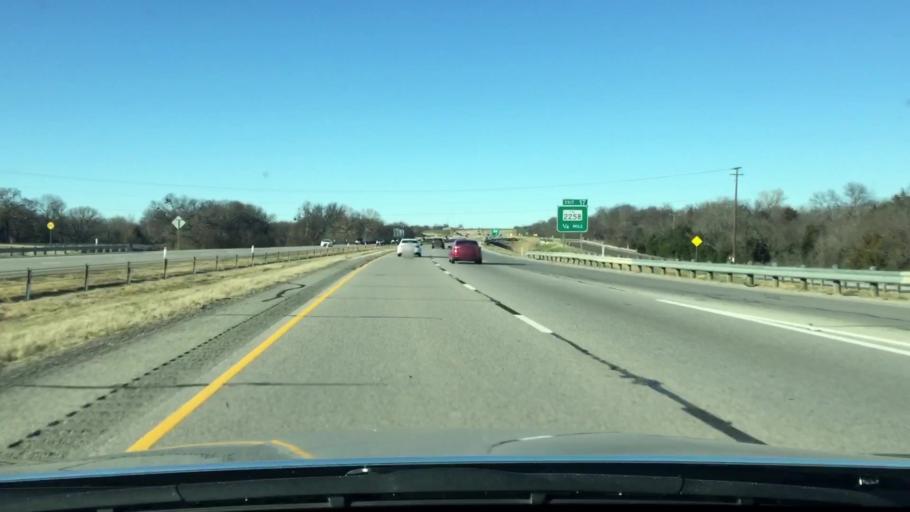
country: US
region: Texas
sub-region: Johnson County
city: Grandview
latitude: 32.2892
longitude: -97.1784
